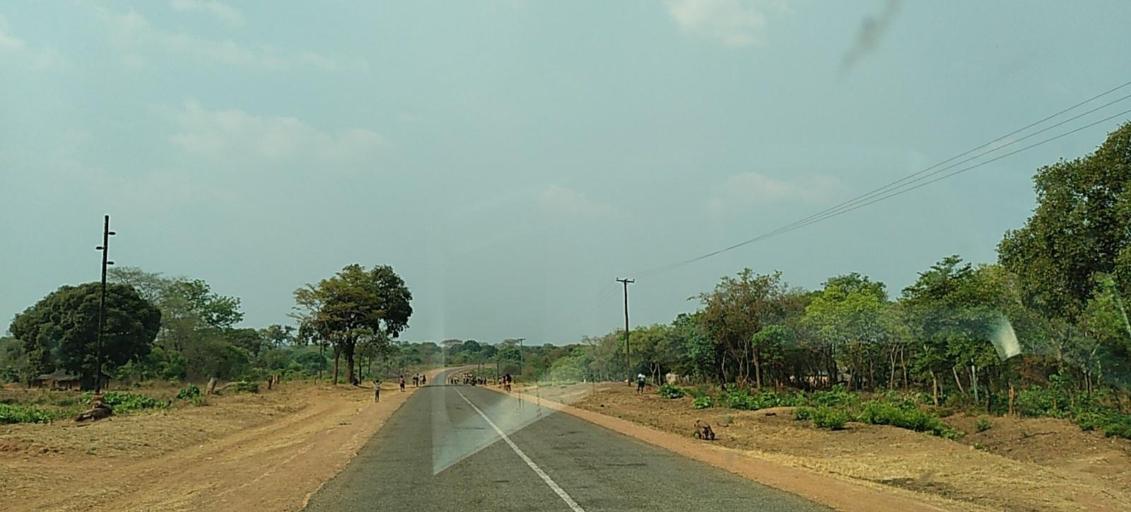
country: ZM
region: North-Western
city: Kabompo
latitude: -13.5400
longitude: 24.2715
